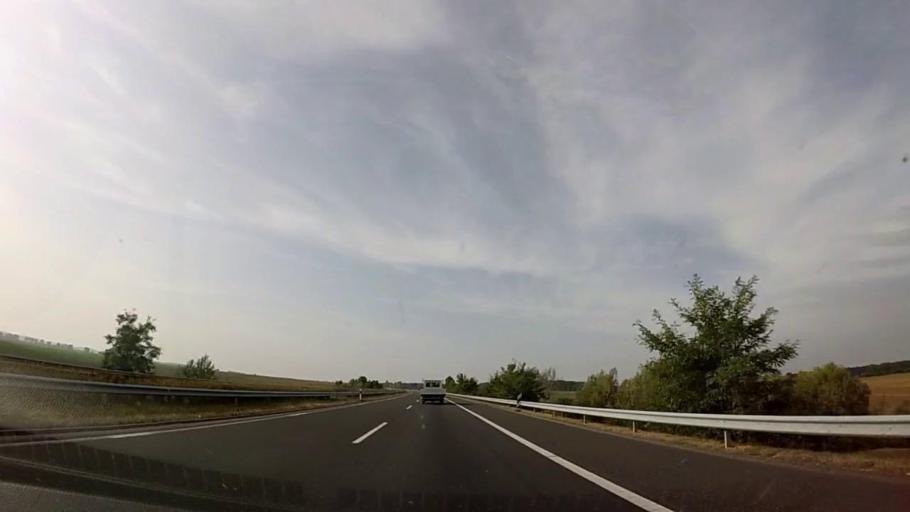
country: HU
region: Somogy
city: Kethely
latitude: 46.6804
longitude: 17.3654
